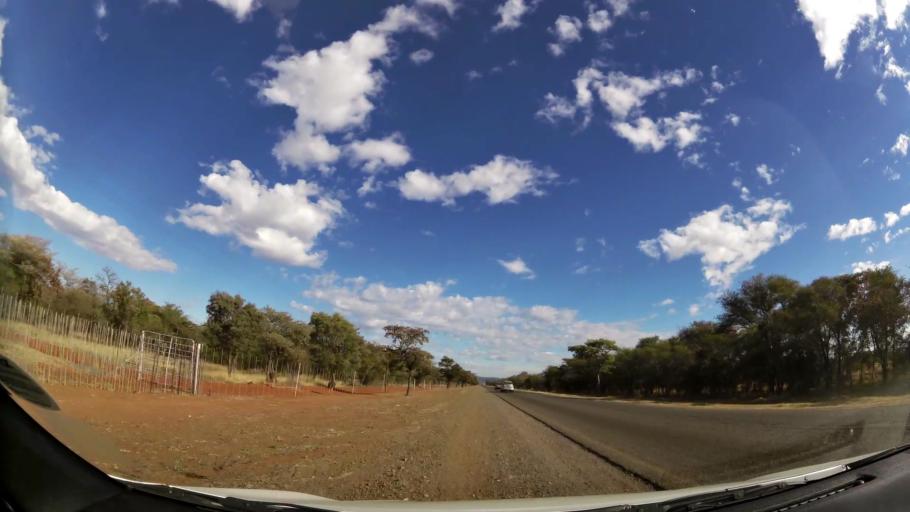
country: ZA
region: Limpopo
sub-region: Waterberg District Municipality
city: Bela-Bela
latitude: -24.9097
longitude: 28.3507
